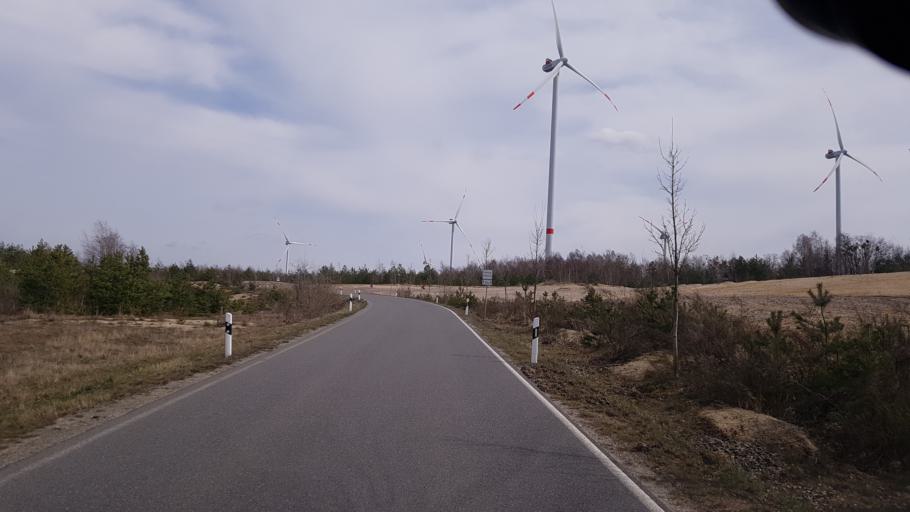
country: DE
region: Brandenburg
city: Schipkau
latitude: 51.5320
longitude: 13.8567
